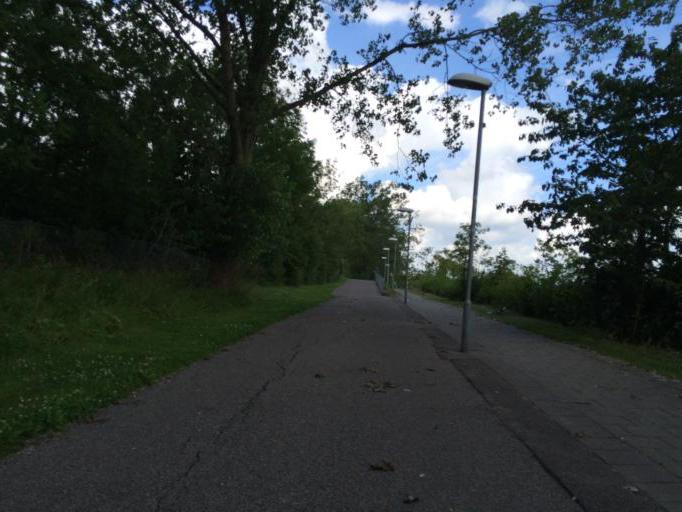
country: DK
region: Capital Region
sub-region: Hoje-Taastrup Kommune
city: Taastrup
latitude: 55.6438
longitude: 12.2821
